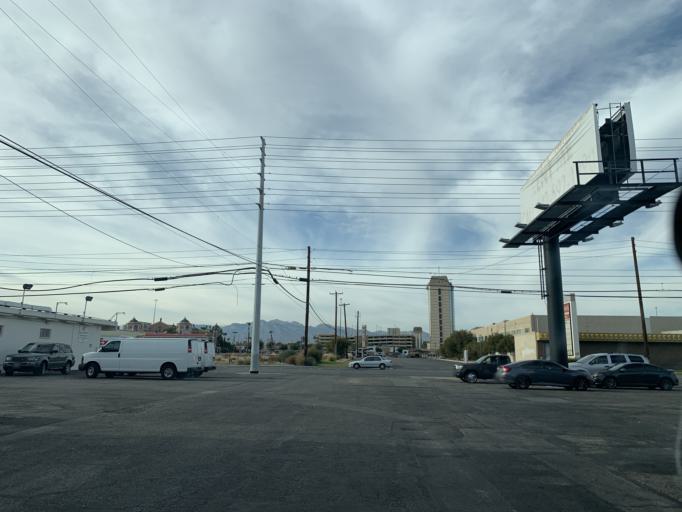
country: US
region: Nevada
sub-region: Clark County
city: Las Vegas
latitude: 36.1398
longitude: -115.1708
